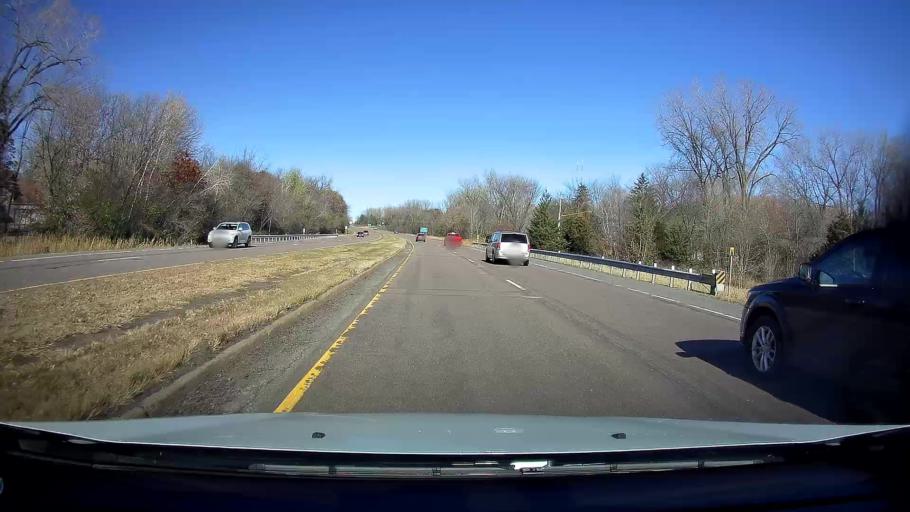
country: US
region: Minnesota
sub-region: Ramsey County
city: Arden Hills
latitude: 45.0416
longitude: -93.1576
